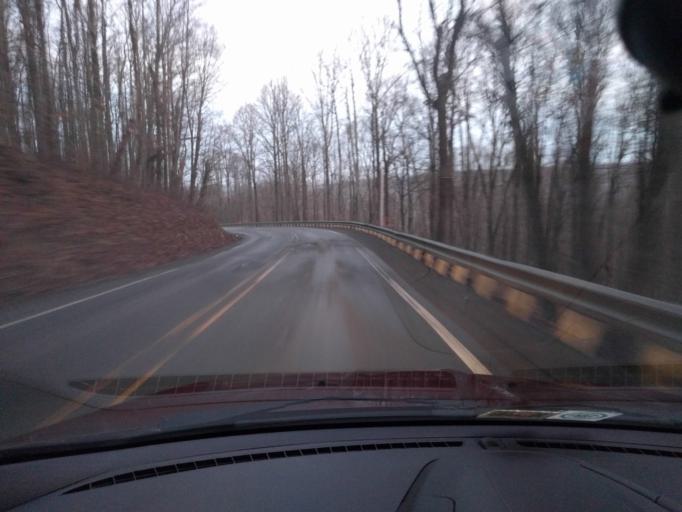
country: US
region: West Virginia
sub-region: Greenbrier County
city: Rainelle
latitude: 37.9882
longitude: -80.8553
